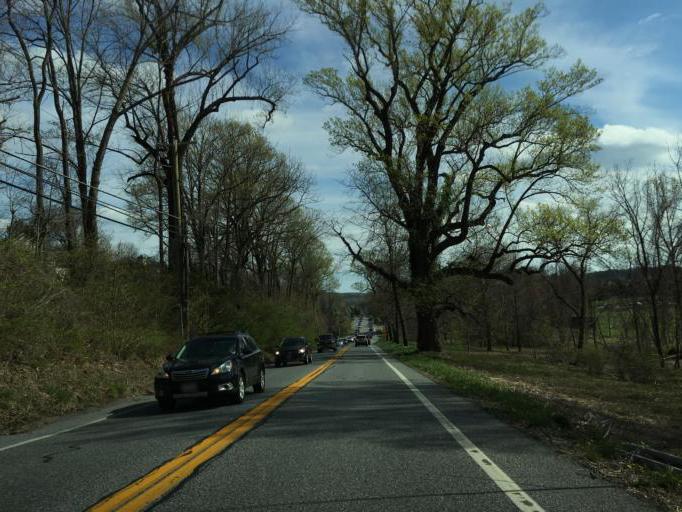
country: US
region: Maryland
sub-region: Baltimore County
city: Mays Chapel
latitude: 39.4293
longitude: -76.6731
